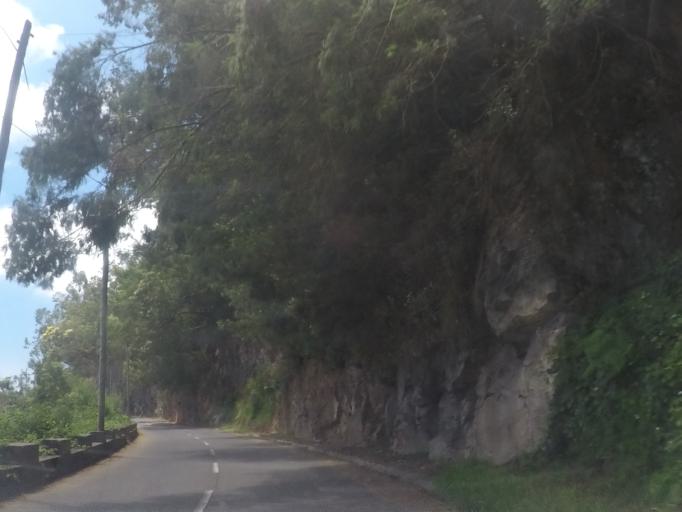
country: PT
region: Madeira
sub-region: Camara de Lobos
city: Curral das Freiras
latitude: 32.6848
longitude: -16.9701
